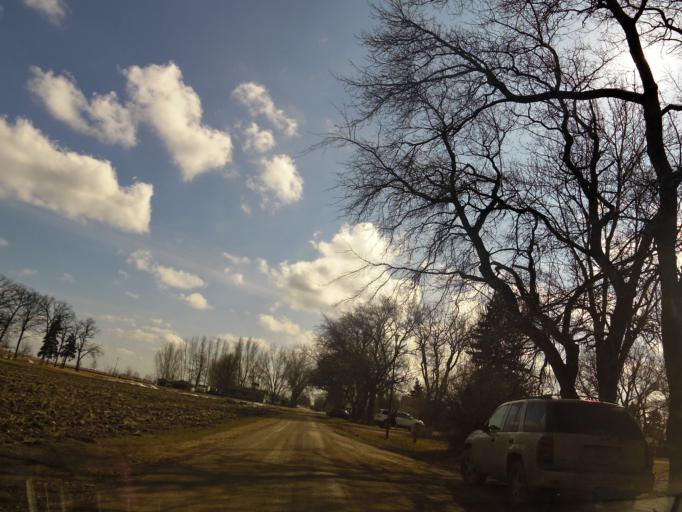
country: US
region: North Dakota
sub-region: Walsh County
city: Grafton
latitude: 48.4229
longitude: -97.3982
